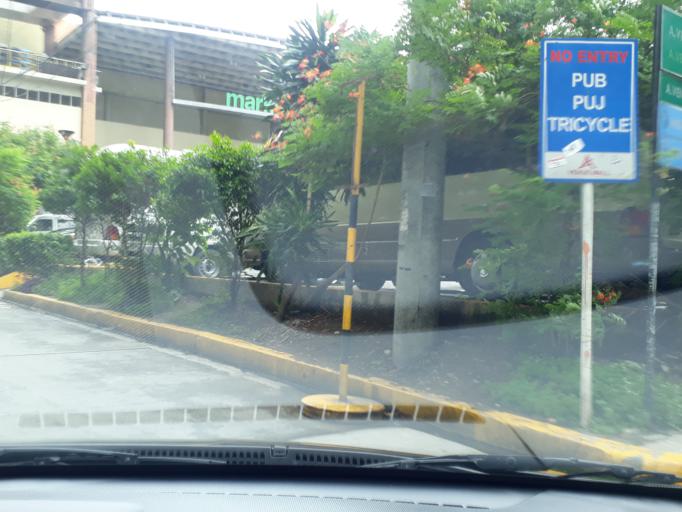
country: PH
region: Metro Manila
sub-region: Makati City
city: Makati City
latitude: 14.5656
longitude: 121.0290
